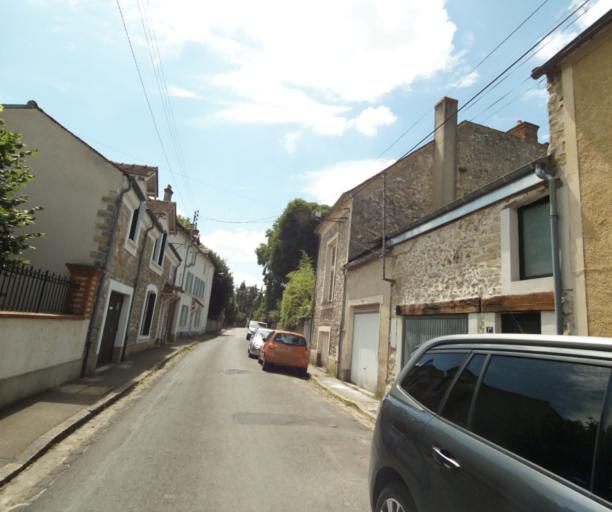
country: FR
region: Ile-de-France
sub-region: Departement de Seine-et-Marne
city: Samois-sur-Seine
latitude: 48.4494
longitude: 2.7498
